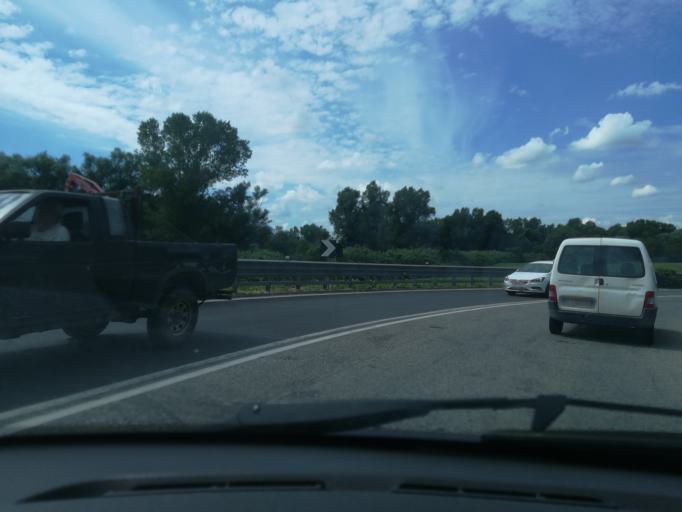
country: IT
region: The Marches
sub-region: Provincia di Macerata
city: Santa Maria Apparente
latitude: 43.2796
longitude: 13.6873
